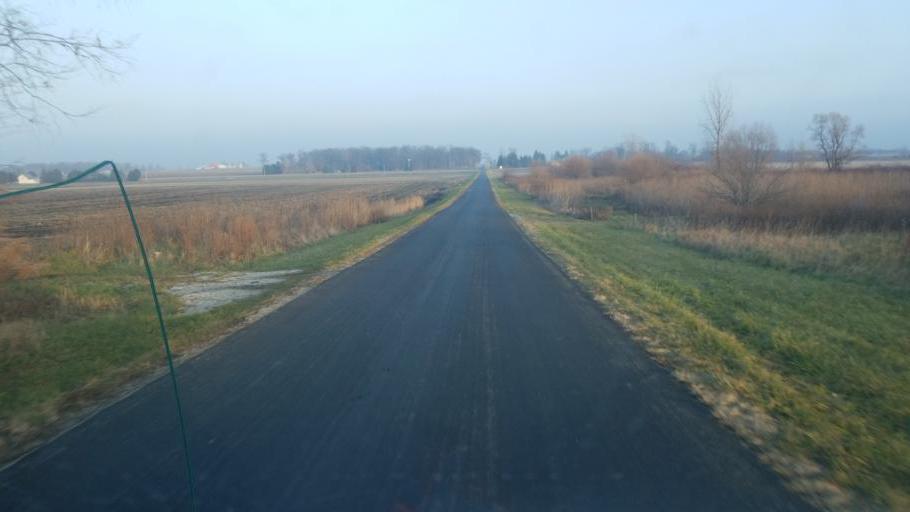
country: US
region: Ohio
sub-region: Wyandot County
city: Carey
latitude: 40.9783
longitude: -83.4002
